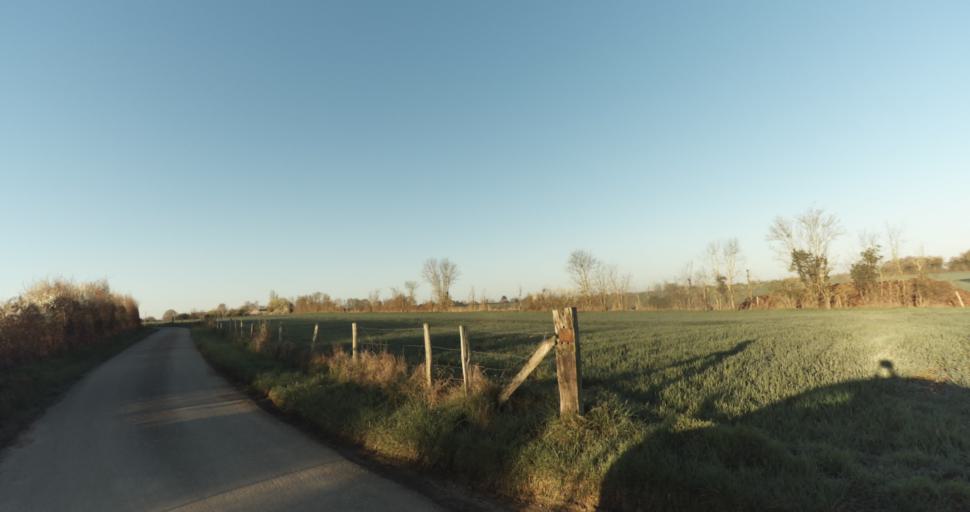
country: FR
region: Lower Normandy
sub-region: Departement du Calvados
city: Saint-Pierre-sur-Dives
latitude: 49.0264
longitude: -0.0168
